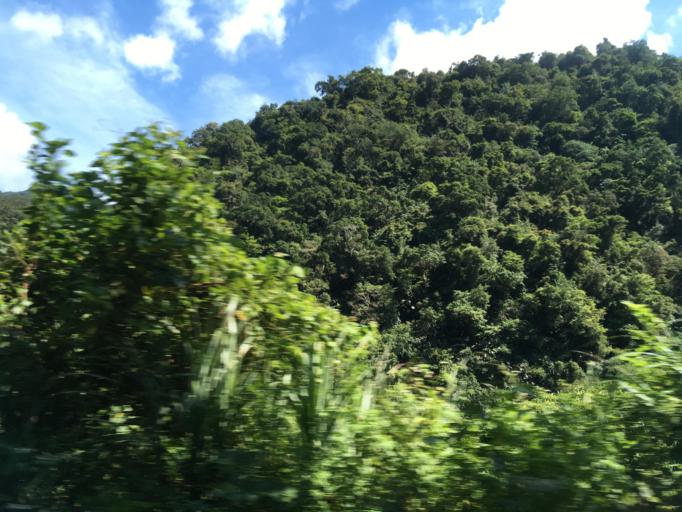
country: TW
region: Taiwan
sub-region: Yilan
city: Yilan
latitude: 24.4244
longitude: 121.7197
